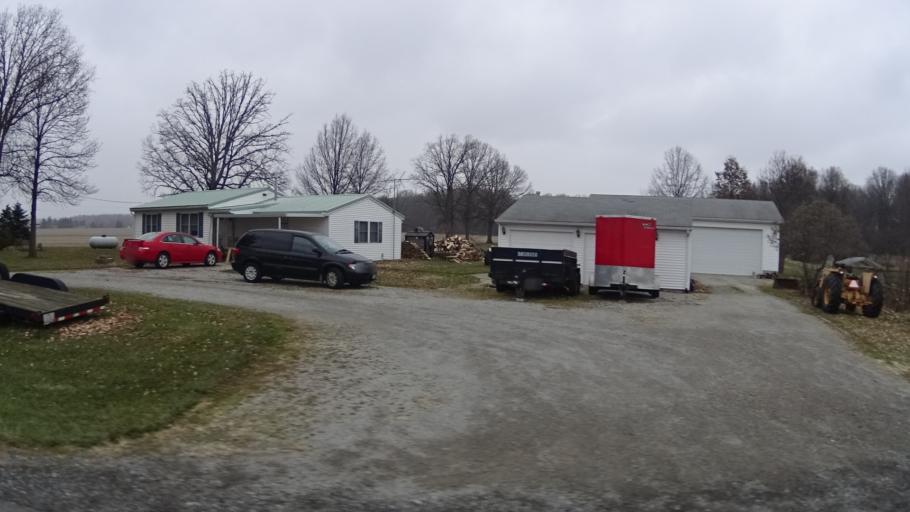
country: US
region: Ohio
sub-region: Lorain County
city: Oberlin
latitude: 41.2916
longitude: -82.2669
